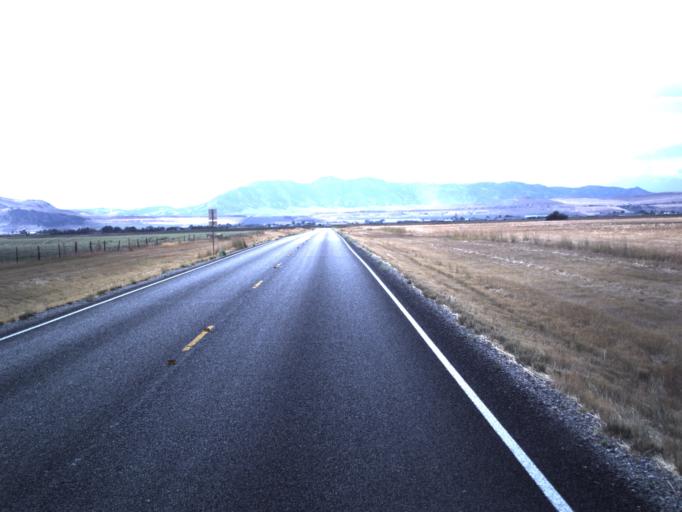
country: US
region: Utah
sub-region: Cache County
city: Lewiston
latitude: 41.9250
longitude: -111.8680
